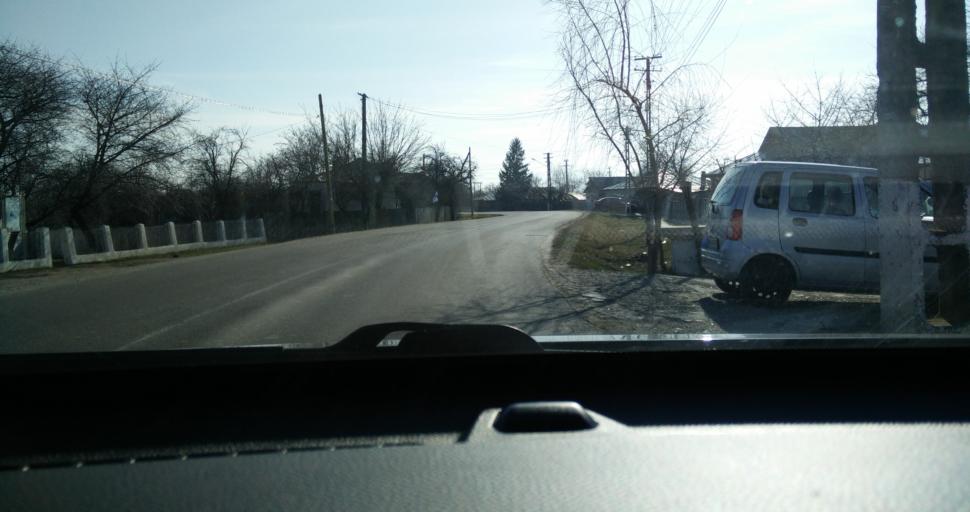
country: RO
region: Vrancea
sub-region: Comuna Nanesti
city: Nanesti
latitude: 45.5485
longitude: 27.5003
